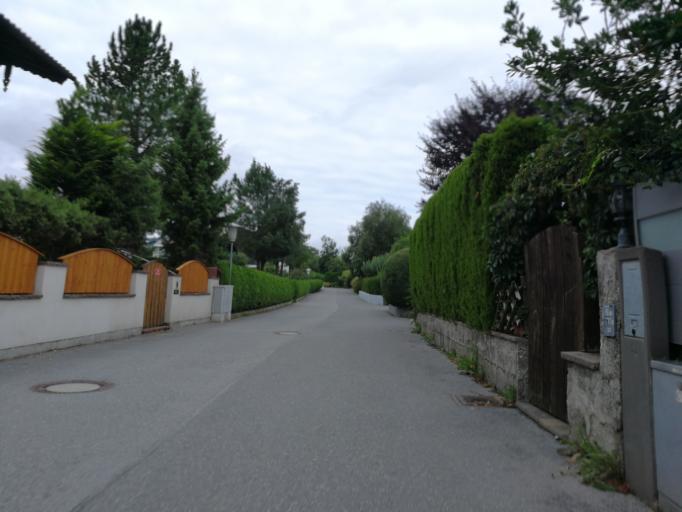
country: DE
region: Bavaria
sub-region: Upper Bavaria
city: Ainring
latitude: 47.7931
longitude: 12.9581
